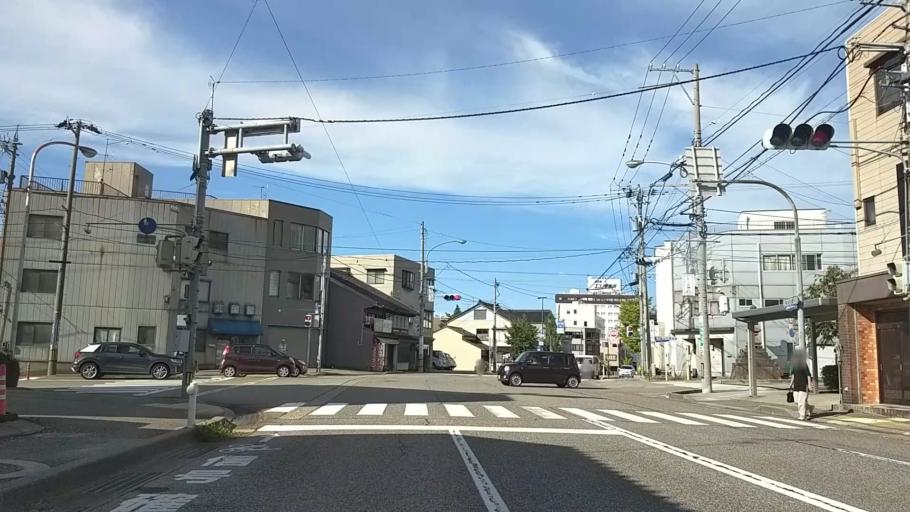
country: JP
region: Ishikawa
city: Kanazawa-shi
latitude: 36.5793
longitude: 136.6702
